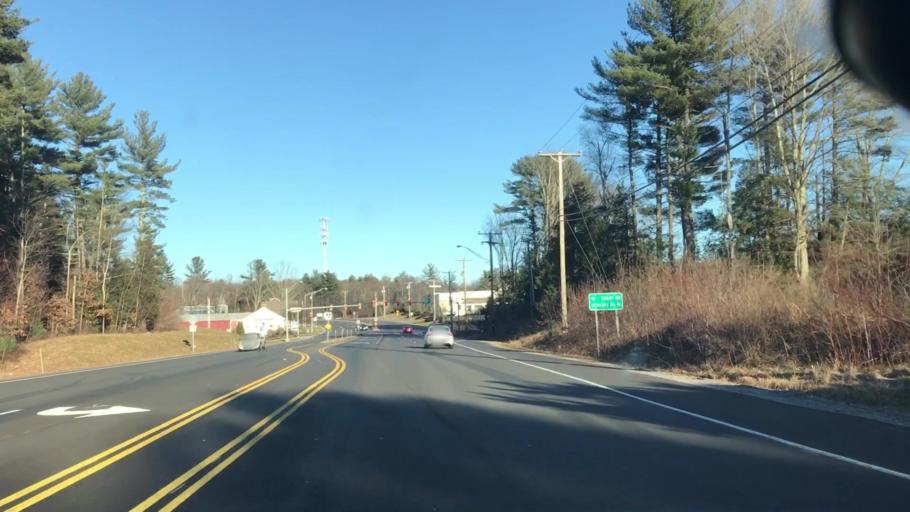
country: US
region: New Hampshire
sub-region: Hillsborough County
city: Bedford
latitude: 42.9207
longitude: -71.5396
